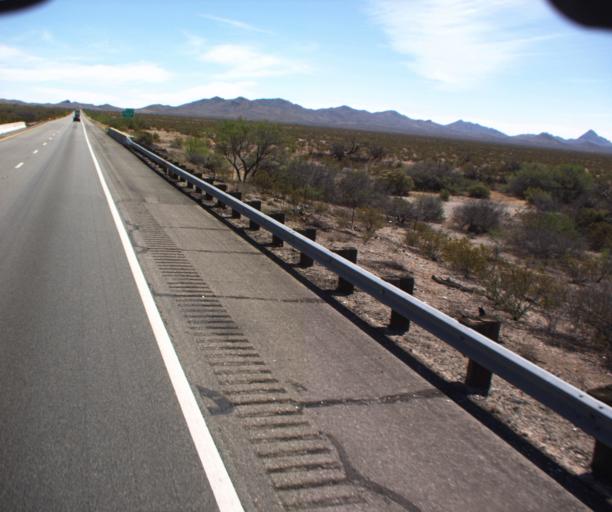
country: US
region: New Mexico
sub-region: Hidalgo County
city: Lordsburg
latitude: 32.2344
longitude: -109.0791
